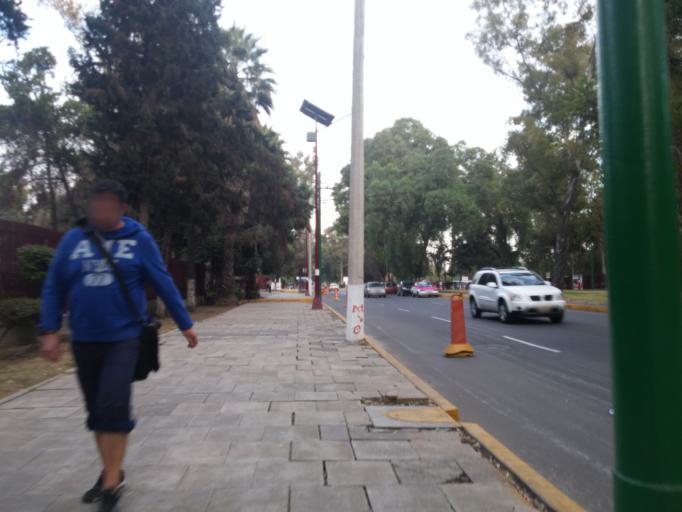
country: MX
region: Mexico
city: Colonia Lindavista
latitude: 19.5047
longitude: -99.1405
